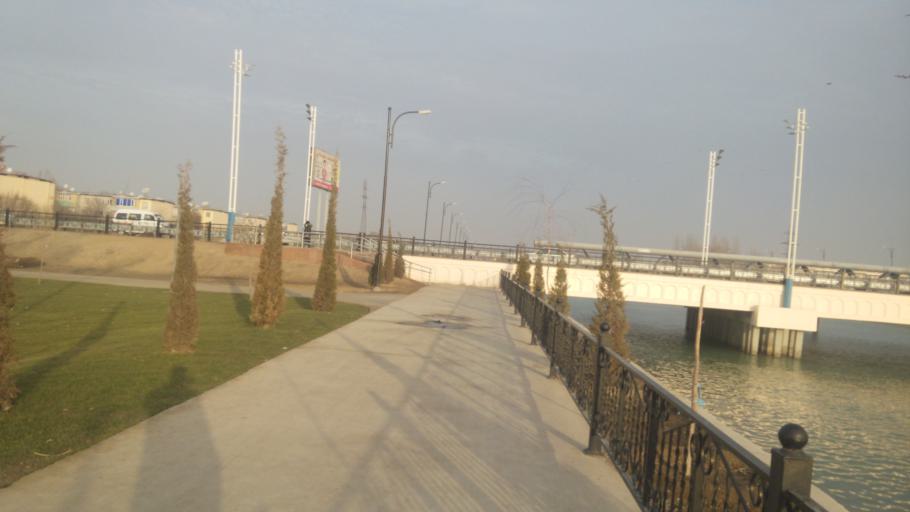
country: UZ
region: Sirdaryo
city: Guliston
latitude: 40.5106
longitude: 68.7772
